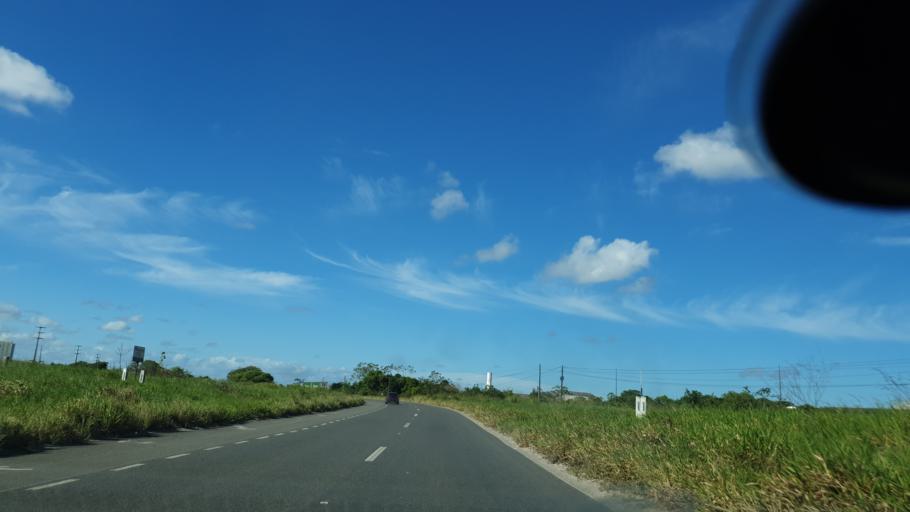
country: BR
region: Bahia
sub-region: Camacari
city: Camacari
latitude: -12.6720
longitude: -38.3000
